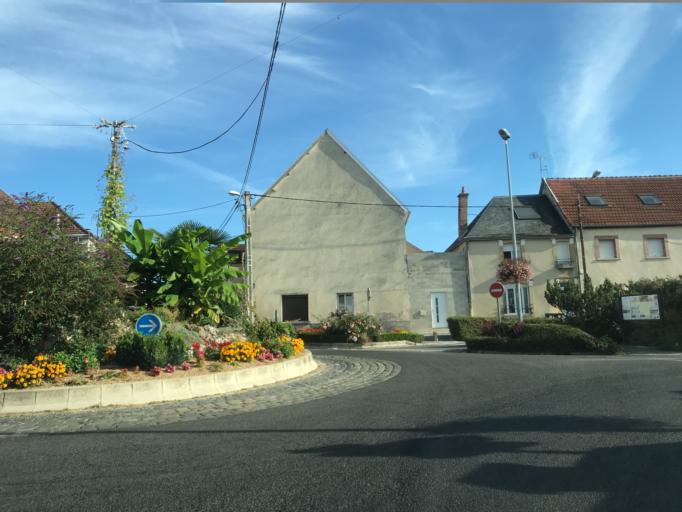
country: FR
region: Champagne-Ardenne
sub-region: Departement de la Marne
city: Damery
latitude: 49.0723
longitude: 3.8780
